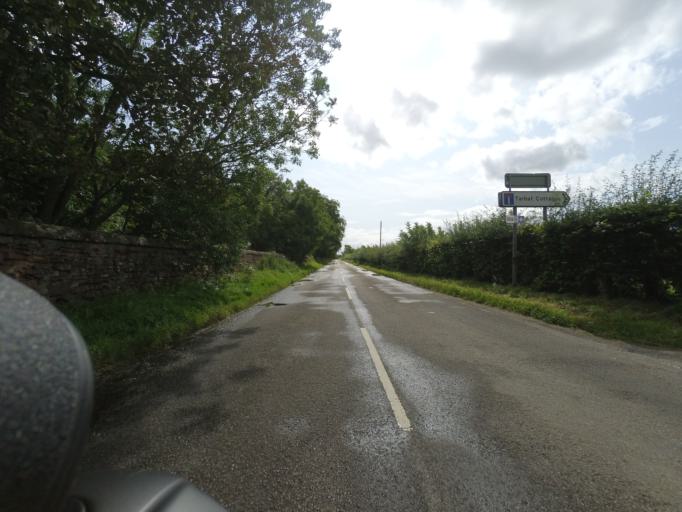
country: GB
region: Scotland
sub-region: Highland
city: Tain
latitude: 57.7390
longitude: -4.0804
